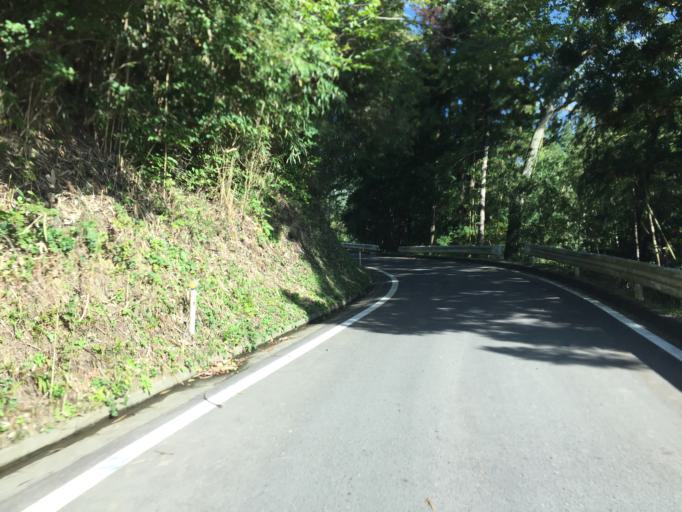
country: JP
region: Fukushima
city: Yanagawamachi-saiwaicho
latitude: 37.8559
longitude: 140.6639
